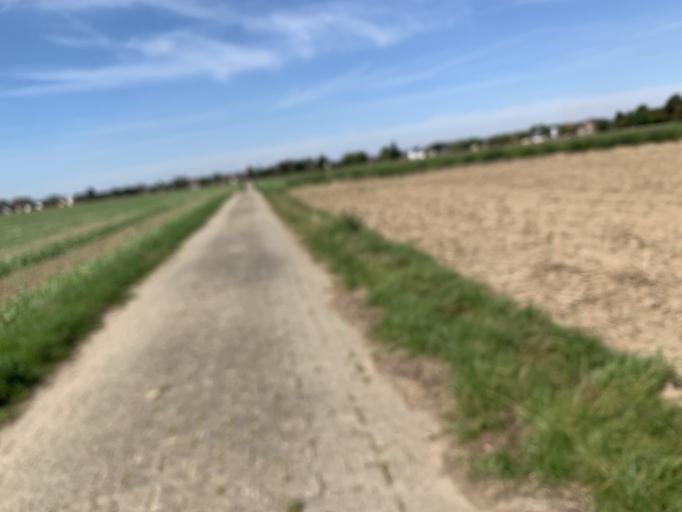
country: DE
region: North Rhine-Westphalia
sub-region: Regierungsbezirk Koln
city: Dueren
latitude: 50.7935
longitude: 6.4373
